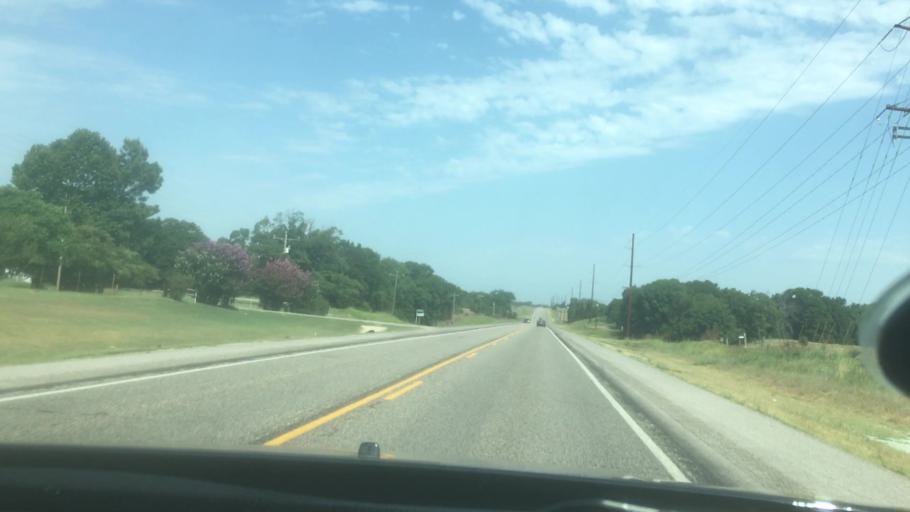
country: US
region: Oklahoma
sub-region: Seminole County
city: Konawa
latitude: 34.8422
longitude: -96.7990
